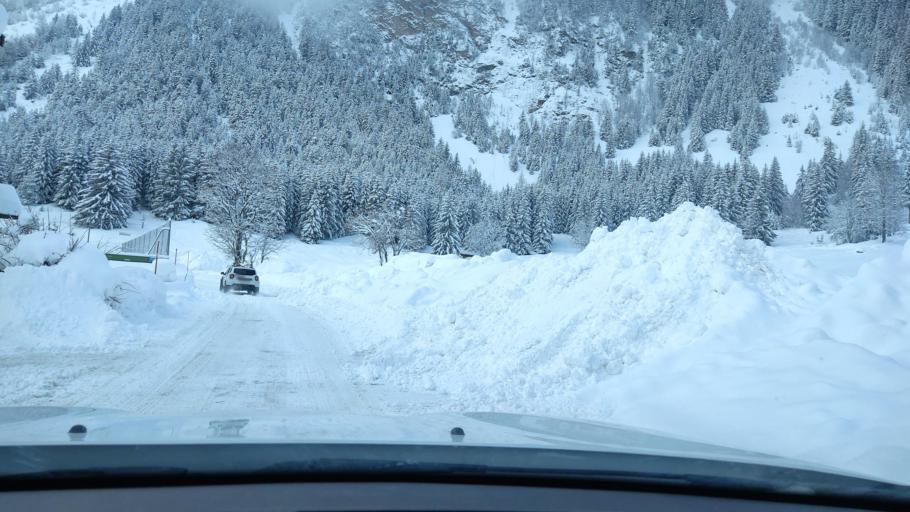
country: FR
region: Rhone-Alpes
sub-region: Departement de la Savoie
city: Courchevel
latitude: 45.3834
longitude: 6.7154
